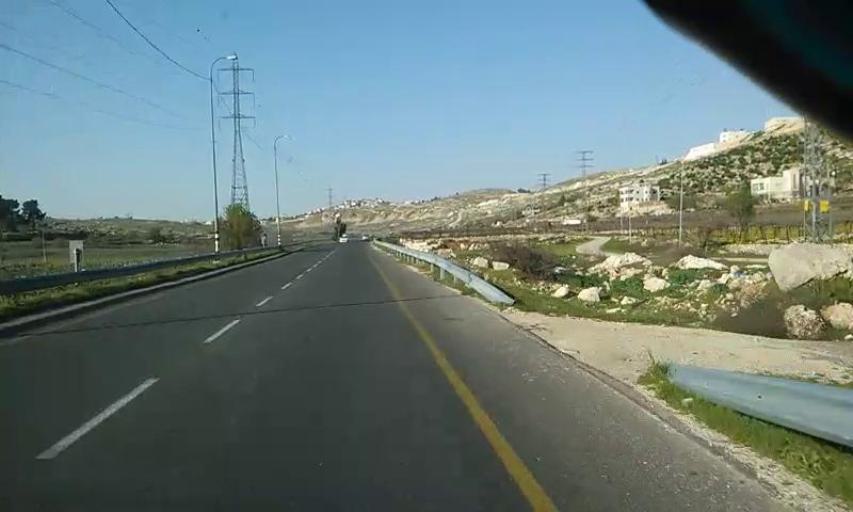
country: PS
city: Al Buq`ah
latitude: 31.5483
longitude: 35.1341
